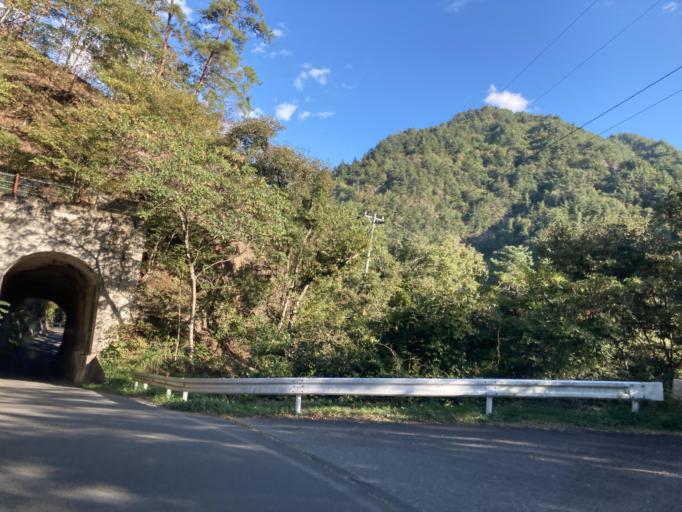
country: JP
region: Nagano
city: Omachi
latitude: 36.4524
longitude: 137.9694
